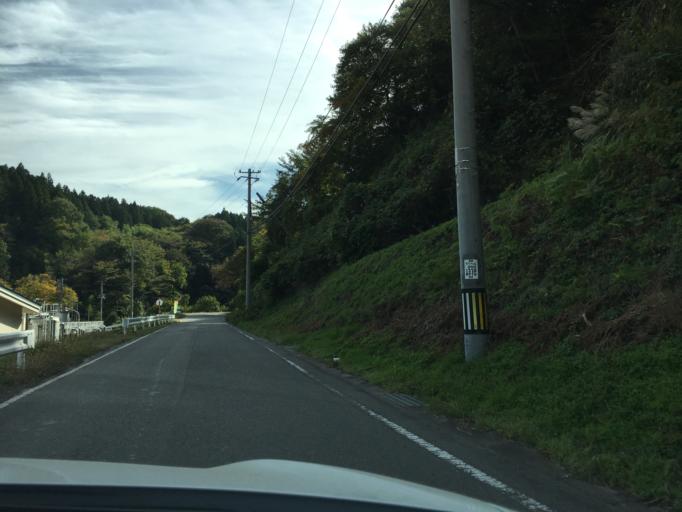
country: JP
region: Fukushima
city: Miharu
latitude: 37.5211
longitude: 140.5050
